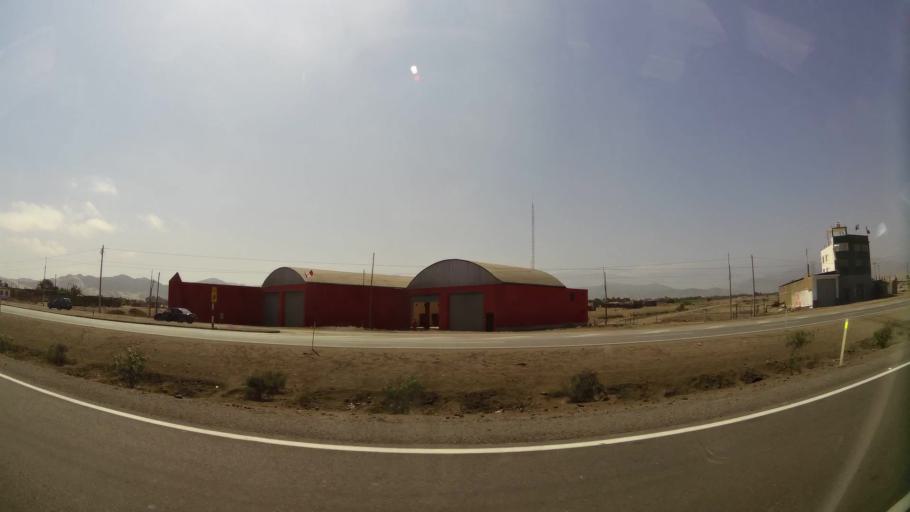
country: PE
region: Lima
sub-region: Provincia de Canete
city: Asia
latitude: -12.7882
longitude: -76.5689
